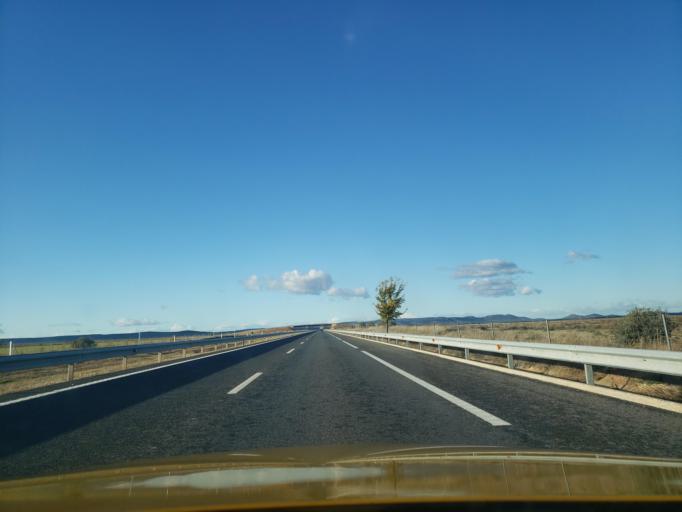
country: ES
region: Castille-La Mancha
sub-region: Province of Toledo
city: Turleque
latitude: 39.5401
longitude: -3.6668
